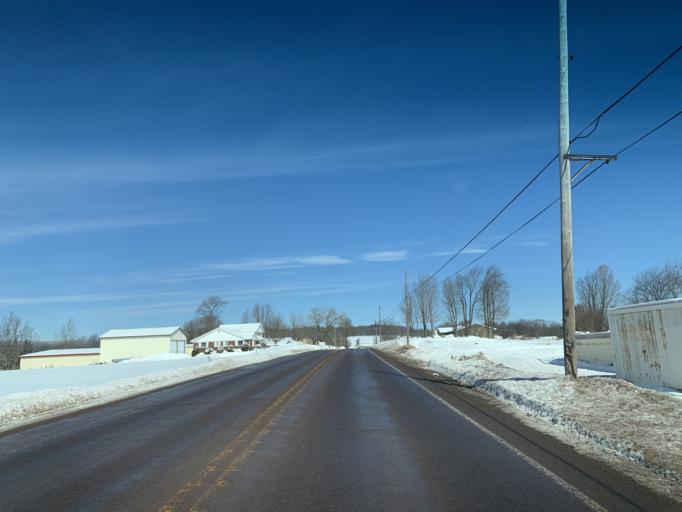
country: US
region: Pennsylvania
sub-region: Somerset County
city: Meyersdale
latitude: 39.7132
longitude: -79.1604
